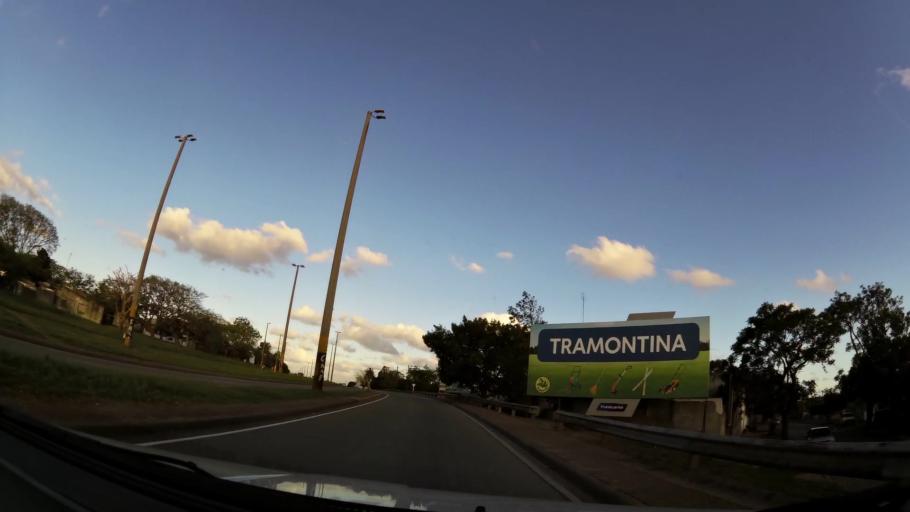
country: UY
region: Montevideo
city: Montevideo
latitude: -34.8730
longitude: -56.2377
